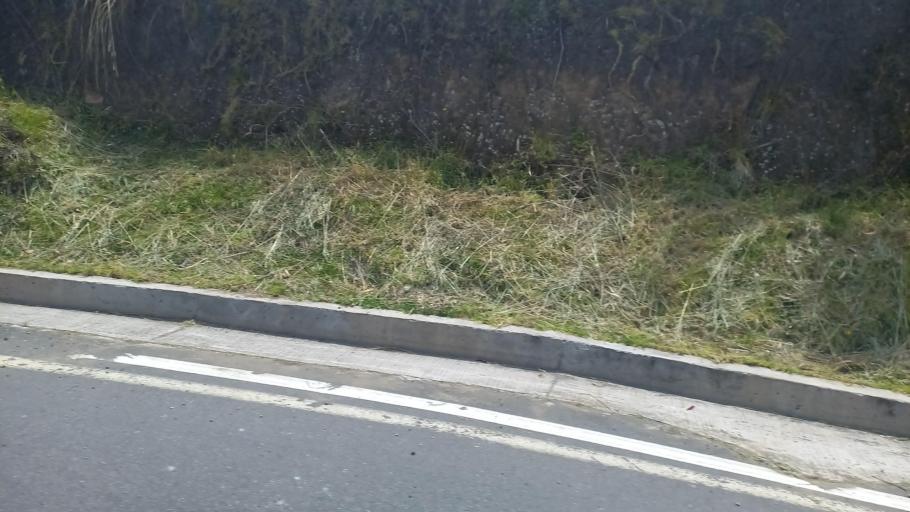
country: EC
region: Pichincha
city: Cayambe
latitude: 0.1802
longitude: -78.0925
